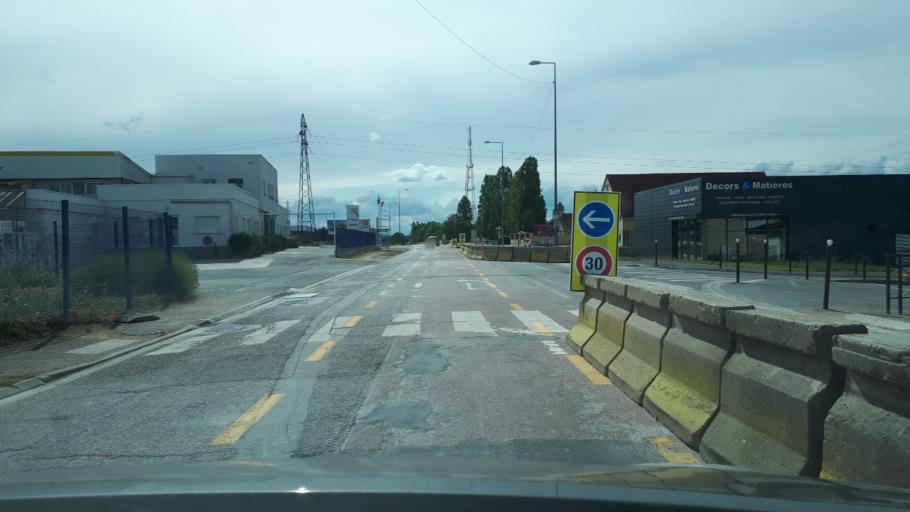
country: FR
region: Centre
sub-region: Departement du Cher
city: Saint-Doulchard
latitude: 47.0819
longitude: 2.3644
